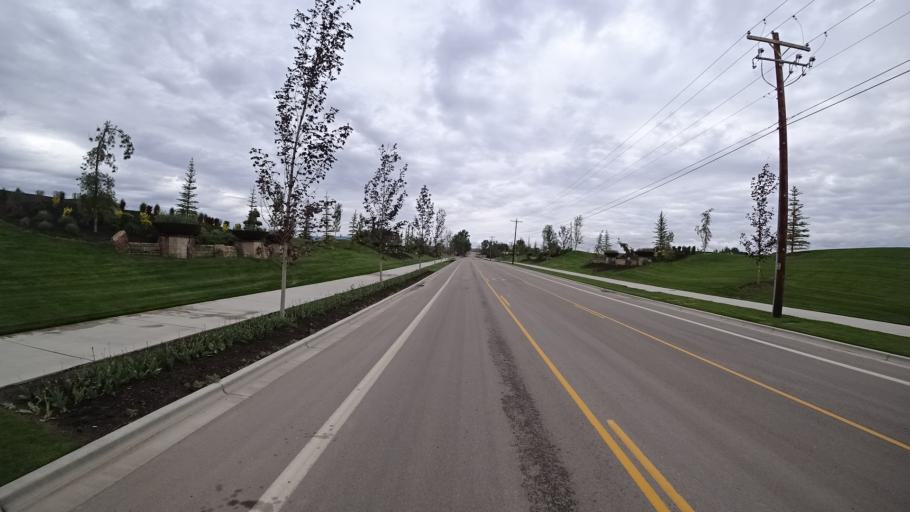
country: US
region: Idaho
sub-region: Ada County
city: Star
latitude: 43.7039
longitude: -116.4435
